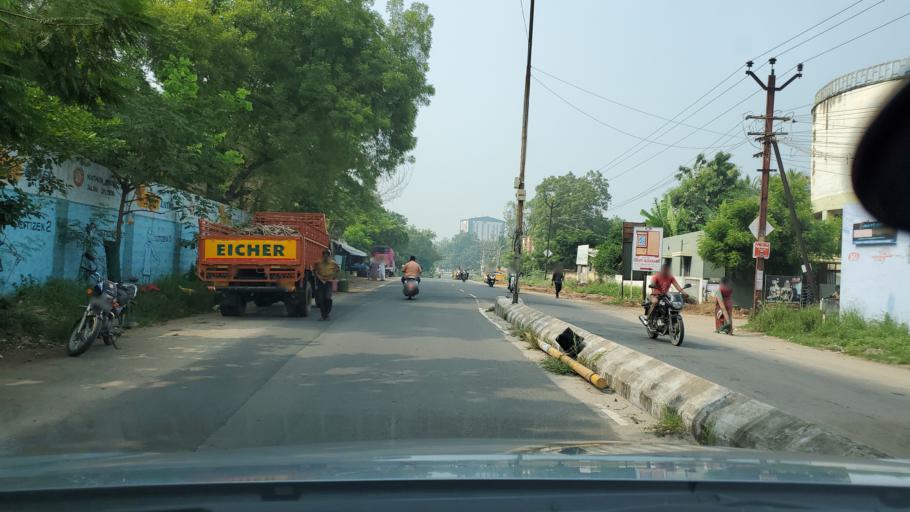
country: IN
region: Tamil Nadu
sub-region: Erode
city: Erode
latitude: 11.3242
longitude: 77.7163
